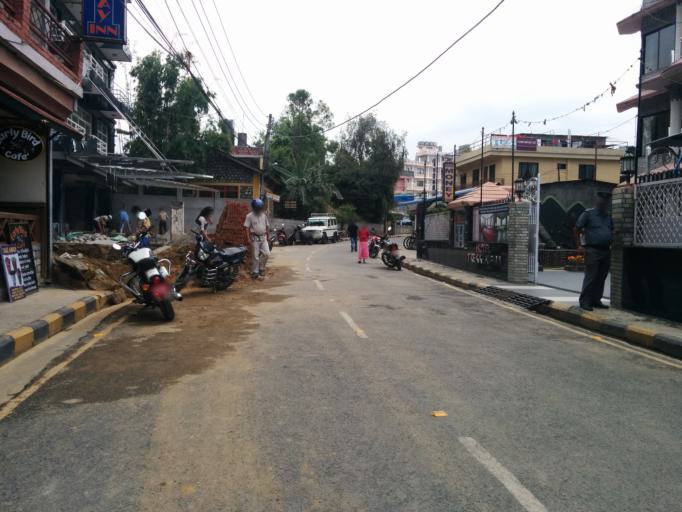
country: NP
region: Western Region
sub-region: Gandaki Zone
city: Pokhara
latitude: 28.2061
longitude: 83.9615
